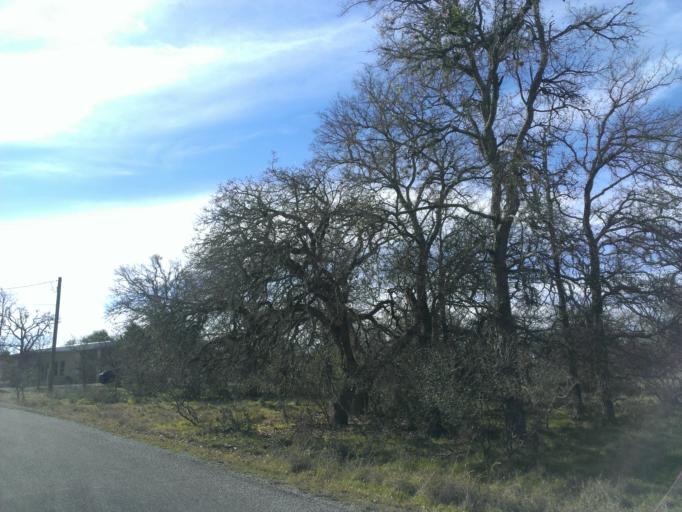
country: US
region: Texas
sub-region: Burnet County
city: Granite Shoals
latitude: 30.6052
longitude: -98.4114
